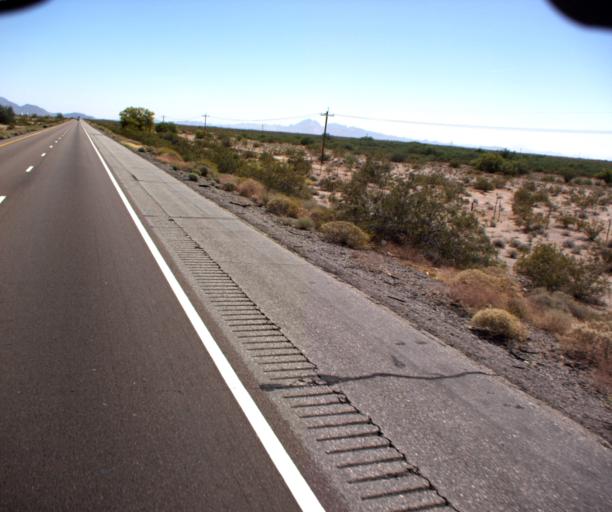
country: US
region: Arizona
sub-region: La Paz County
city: Salome
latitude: 33.5562
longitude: -113.2706
